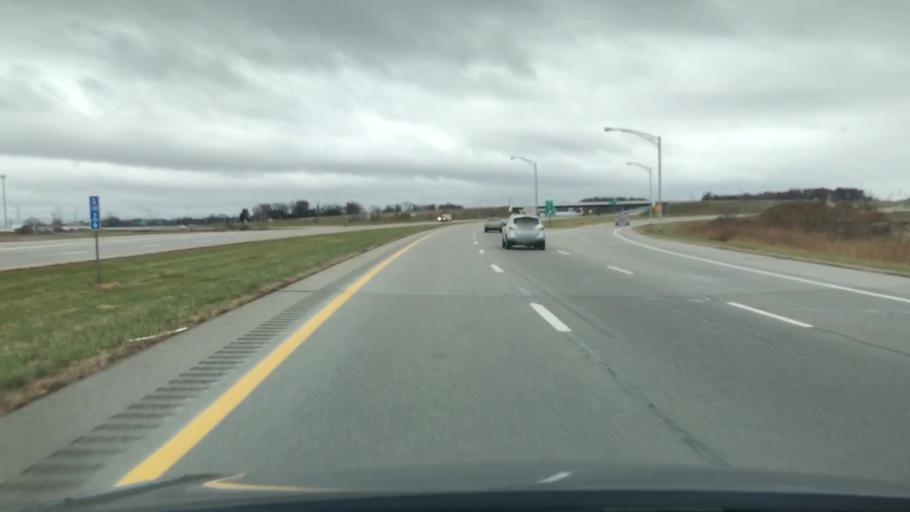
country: US
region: Ohio
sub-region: Wood County
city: Millbury
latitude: 41.5640
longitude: -83.4589
